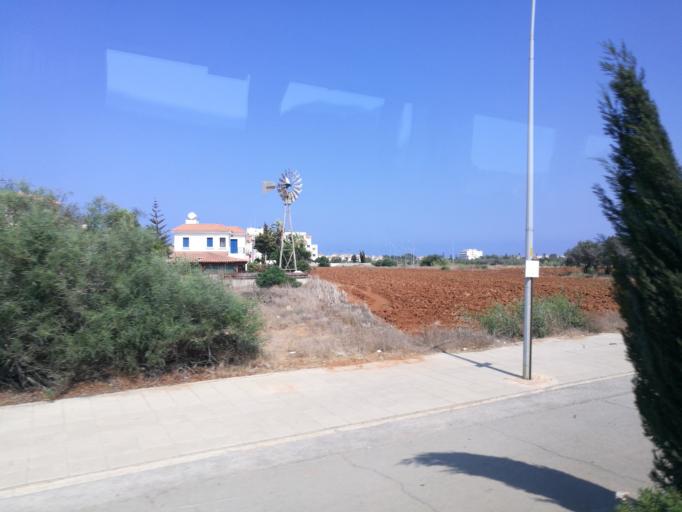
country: CY
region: Ammochostos
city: Protaras
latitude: 35.0313
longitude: 34.0287
